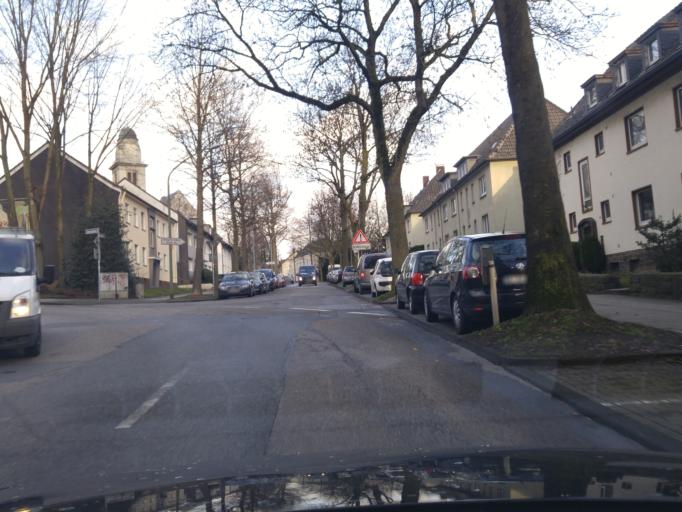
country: DE
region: North Rhine-Westphalia
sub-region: Regierungsbezirk Dusseldorf
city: Essen
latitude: 51.4516
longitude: 7.0757
